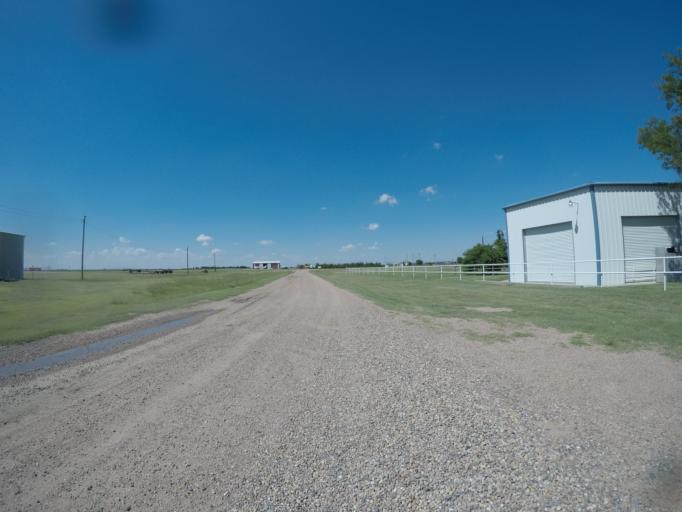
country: US
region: Kansas
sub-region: Sheridan County
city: Hoxie
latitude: 39.3595
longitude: -100.4405
